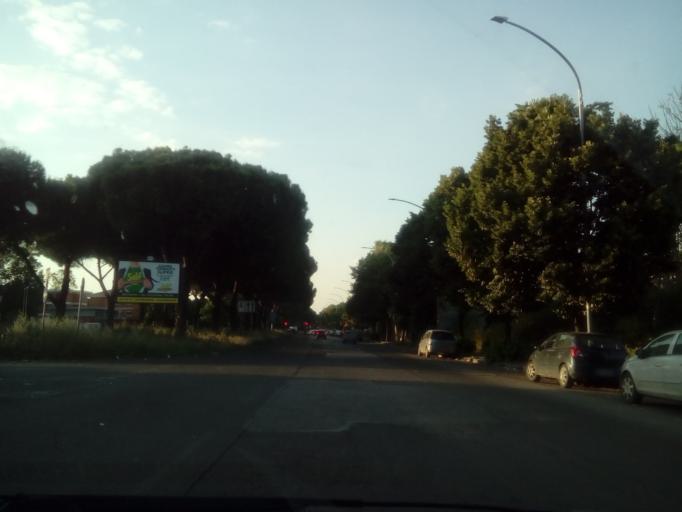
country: IT
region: Latium
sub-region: Citta metropolitana di Roma Capitale
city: Rome
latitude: 41.8818
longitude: 12.5734
